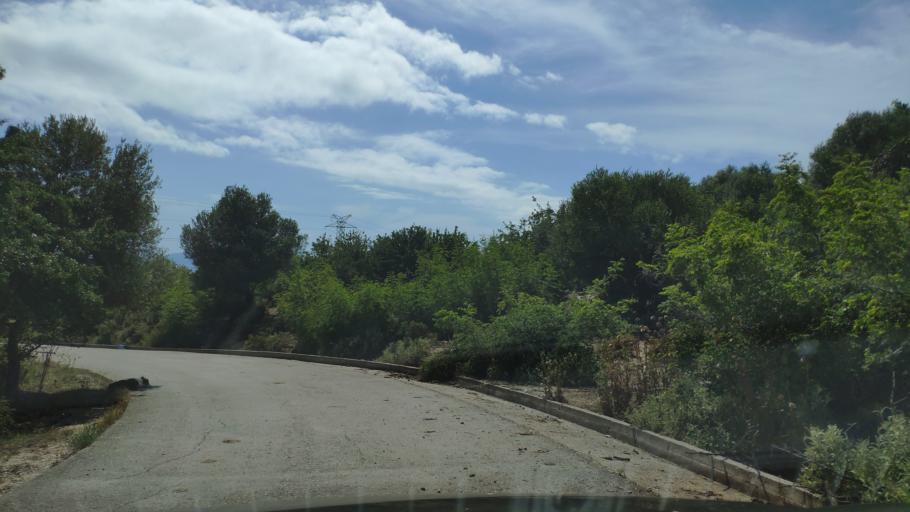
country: AL
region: Vlore
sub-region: Rrethi i Sarandes
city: Konispol
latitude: 39.6281
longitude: 20.2098
